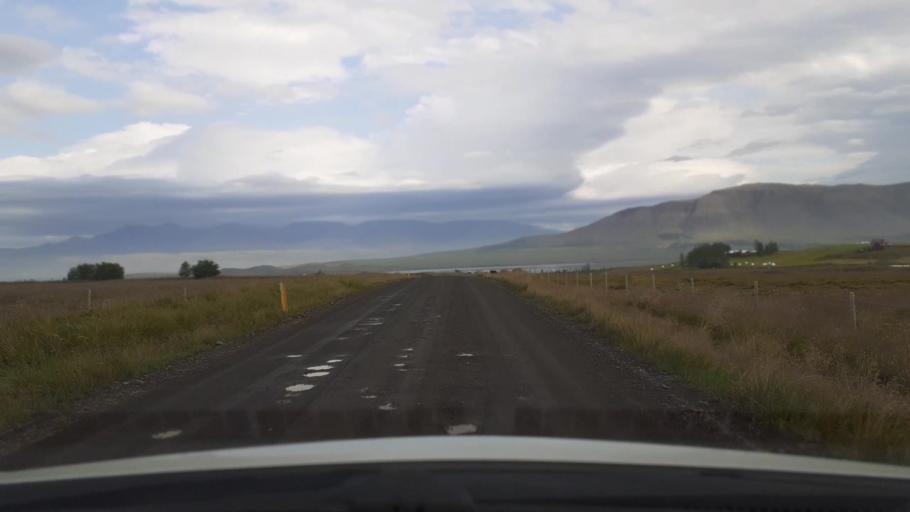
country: IS
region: Capital Region
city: Mosfellsbaer
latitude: 64.3217
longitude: -21.6497
